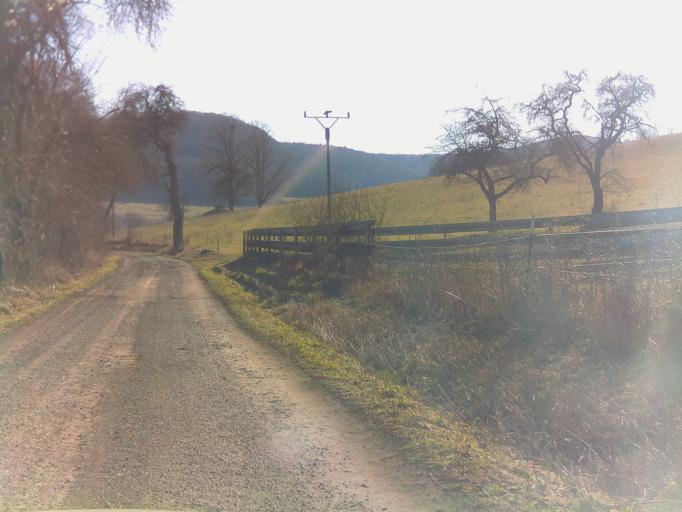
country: DE
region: Thuringia
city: Belrieth
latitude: 50.5375
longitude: 10.5001
